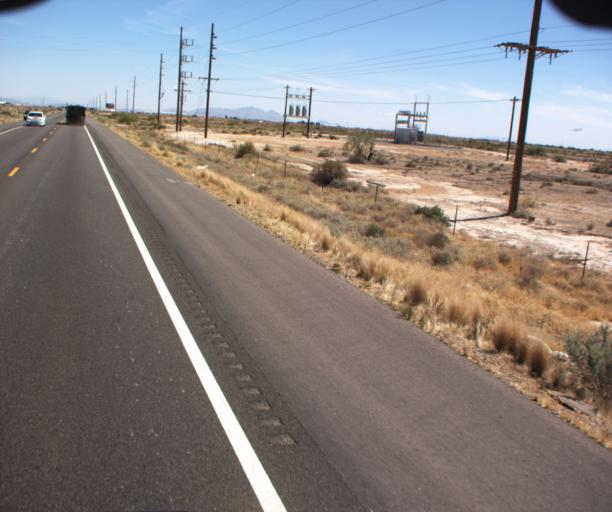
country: US
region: Arizona
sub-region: Pinal County
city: Blackwater
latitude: 33.0080
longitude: -111.6183
